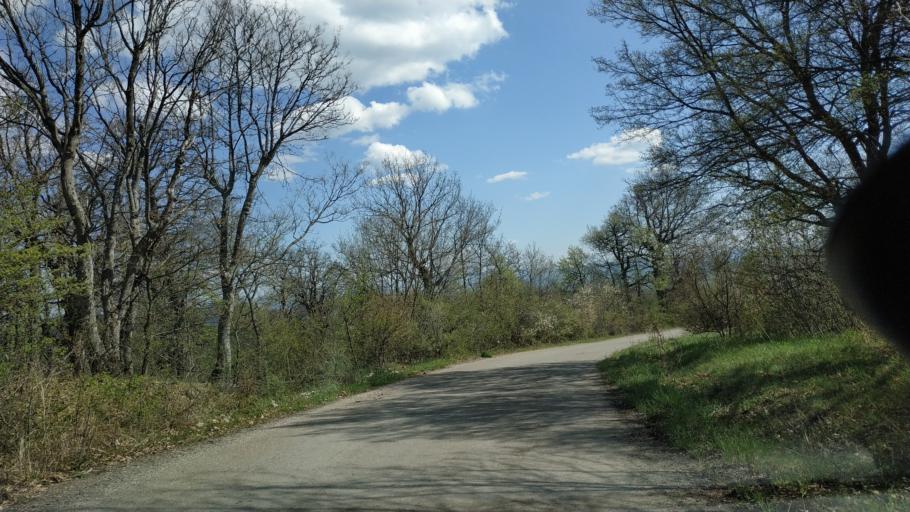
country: RS
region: Central Serbia
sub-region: Zajecarski Okrug
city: Soko Banja
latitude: 43.5527
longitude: 21.8972
